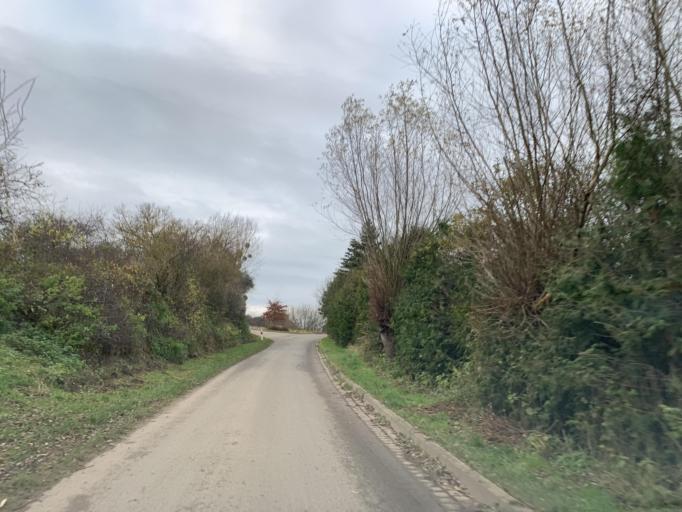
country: DE
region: Mecklenburg-Vorpommern
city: Carpin
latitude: 53.4022
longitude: 13.2016
